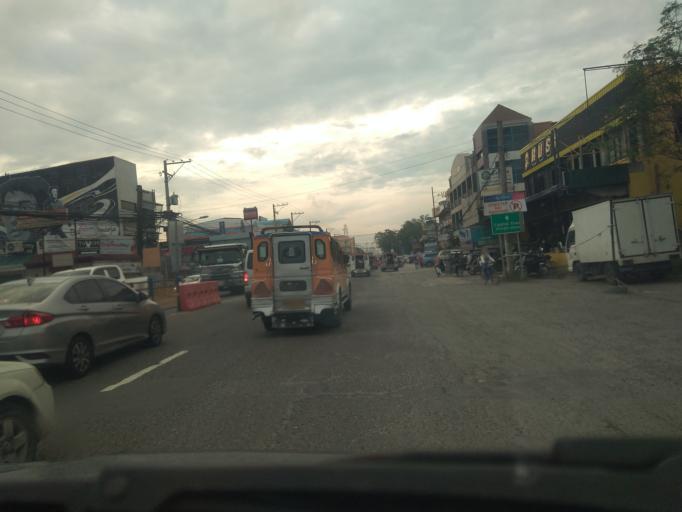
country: PH
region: Central Luzon
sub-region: Province of Pampanga
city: San Fernando
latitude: 15.0382
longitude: 120.6816
